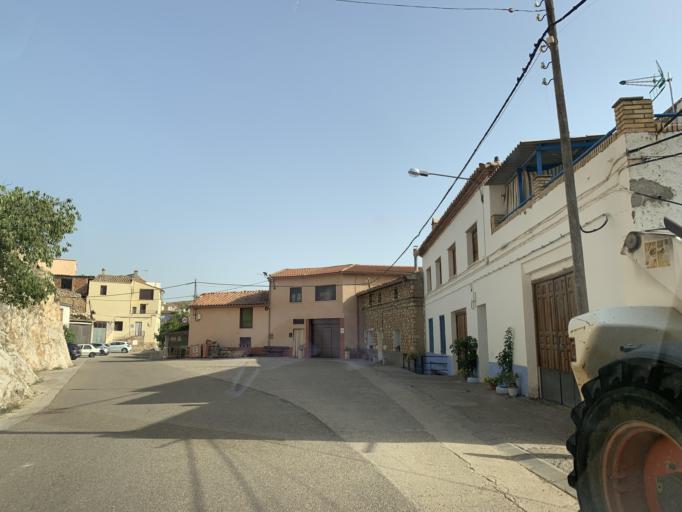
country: ES
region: Aragon
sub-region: Provincia de Zaragoza
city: Almonacid de la Cuba
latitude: 41.2781
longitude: -0.7916
